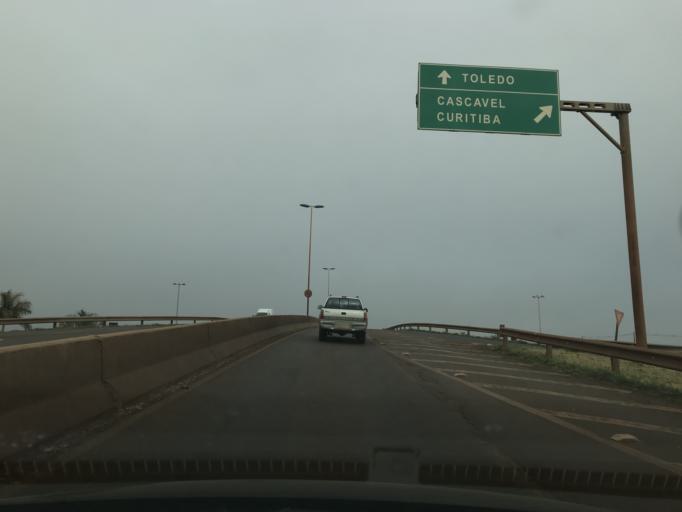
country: BR
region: Parana
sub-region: Toledo
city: Toledo
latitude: -24.7176
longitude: -53.7104
